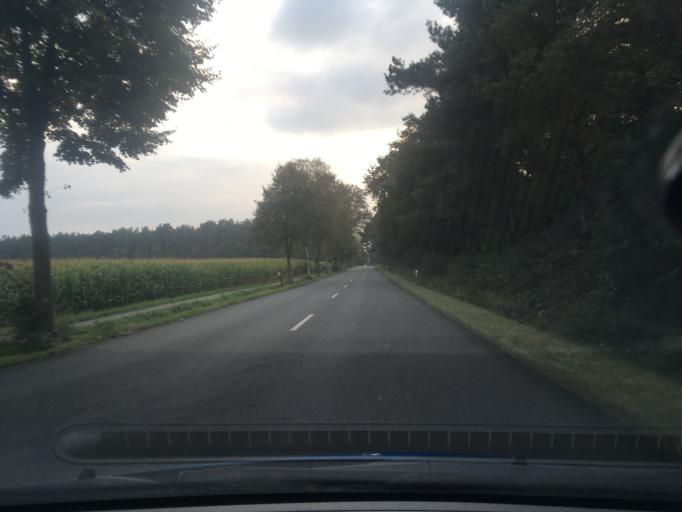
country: DE
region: Lower Saxony
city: Soderstorf
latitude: 53.1240
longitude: 10.1025
